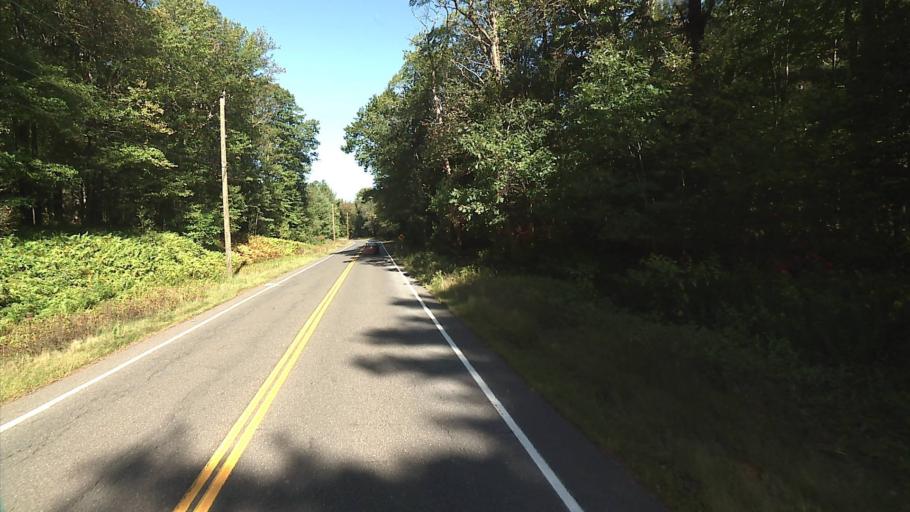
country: US
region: Connecticut
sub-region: Hartford County
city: Bristol
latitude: 41.7391
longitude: -72.9632
